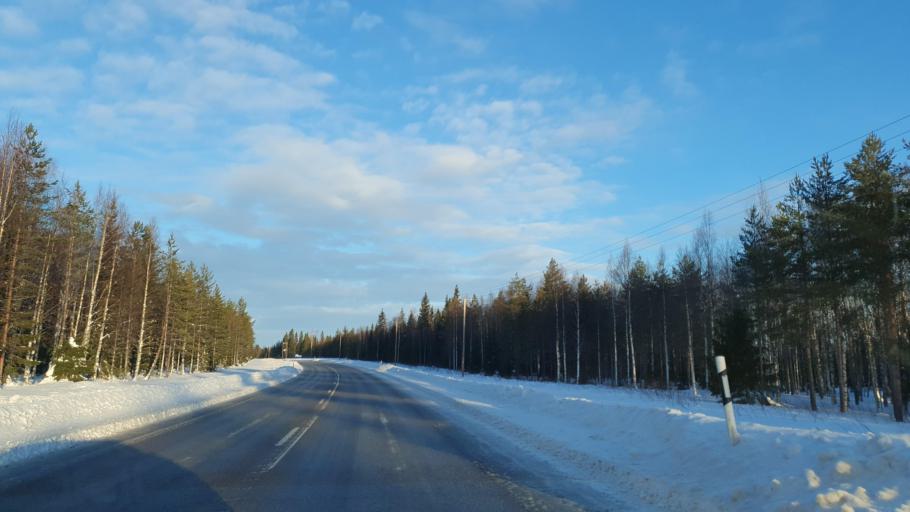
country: FI
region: Kainuu
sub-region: Kajaani
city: Vaala
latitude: 64.5283
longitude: 27.2696
